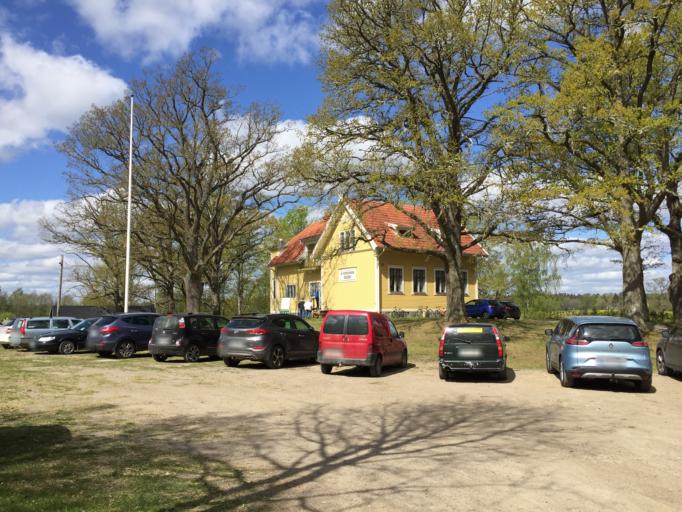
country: SE
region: OEstergoetland
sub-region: Finspangs Kommun
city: Finspang
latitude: 58.8941
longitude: 15.7008
